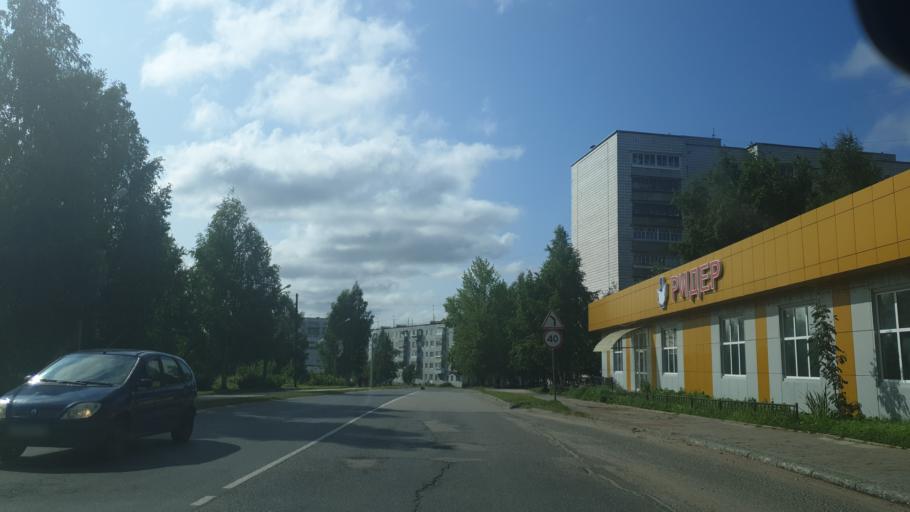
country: RU
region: Komi Republic
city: Ezhva
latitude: 61.7918
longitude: 50.7500
